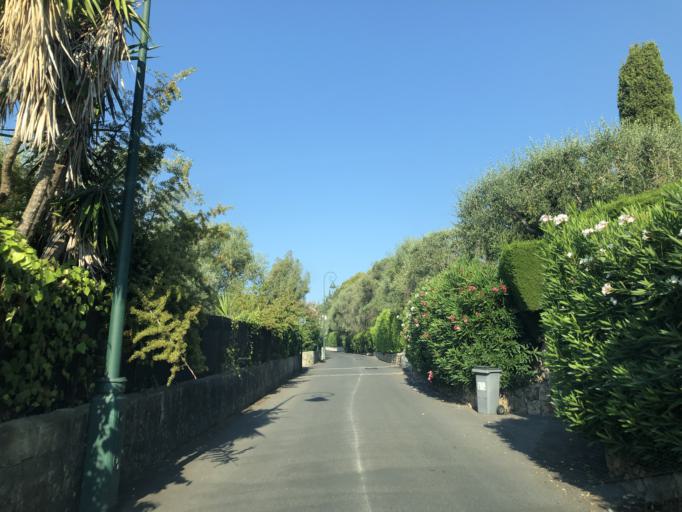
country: FR
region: Provence-Alpes-Cote d'Azur
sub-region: Departement des Alpes-Maritimes
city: Biot
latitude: 43.6238
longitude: 7.0892
